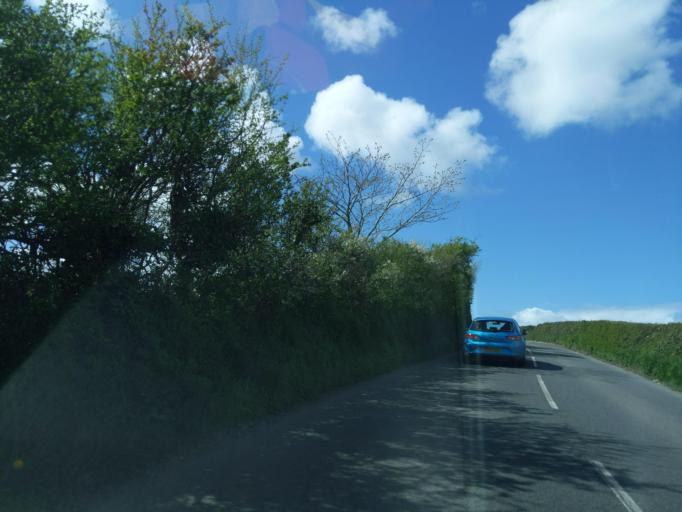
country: GB
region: England
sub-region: Cornwall
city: Wadebridge
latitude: 50.5416
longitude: -4.8600
